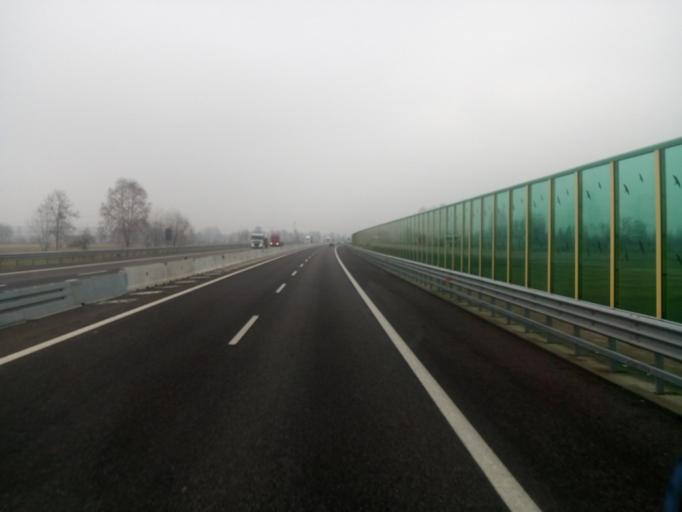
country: IT
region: Lombardy
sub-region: Provincia di Brescia
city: Flero
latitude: 45.4743
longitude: 10.1853
